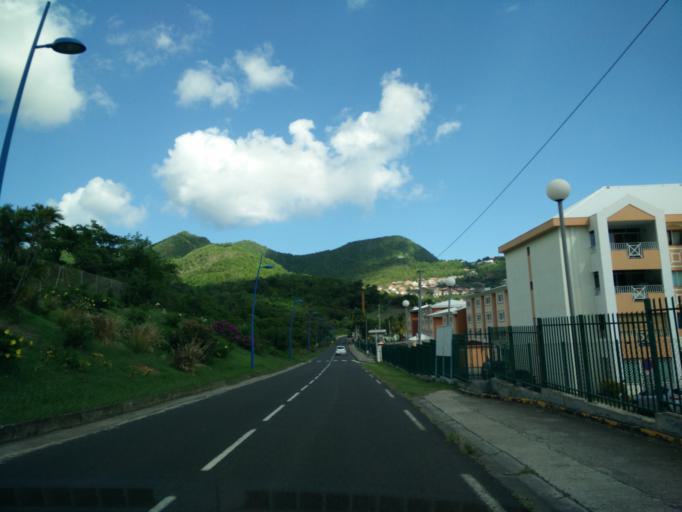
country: MQ
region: Martinique
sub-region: Martinique
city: Les Trois-Ilets
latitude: 14.4978
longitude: -61.0791
